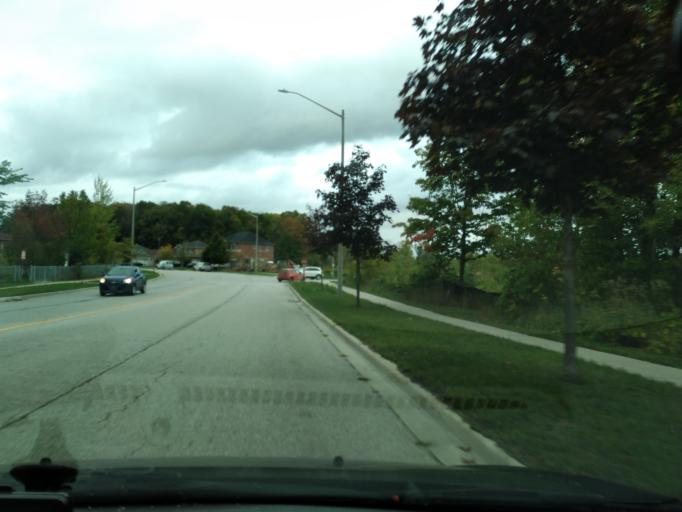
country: CA
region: Ontario
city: Innisfil
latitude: 44.3021
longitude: -79.5596
